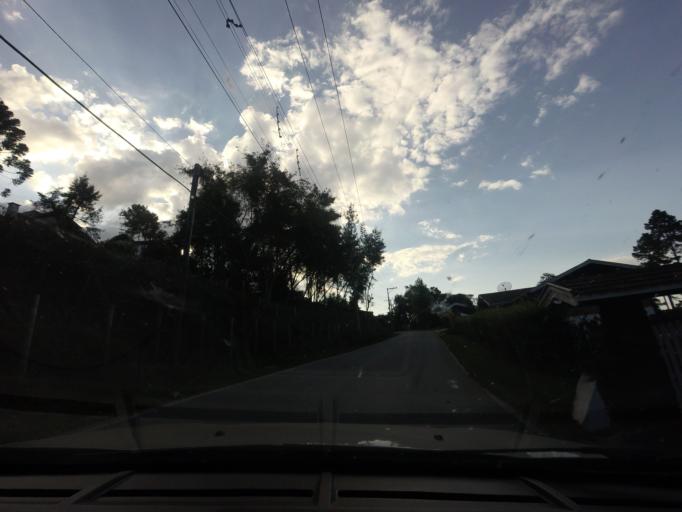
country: BR
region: Sao Paulo
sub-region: Campos Do Jordao
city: Campos do Jordao
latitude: -22.7453
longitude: -45.5665
